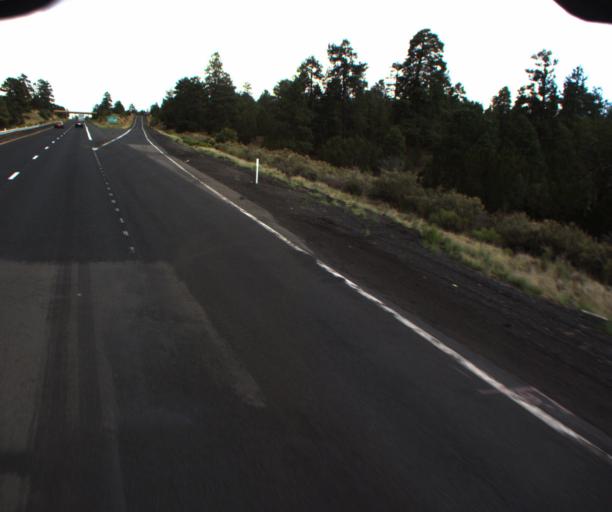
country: US
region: Arizona
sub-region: Coconino County
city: Flagstaff
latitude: 35.2096
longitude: -111.5227
